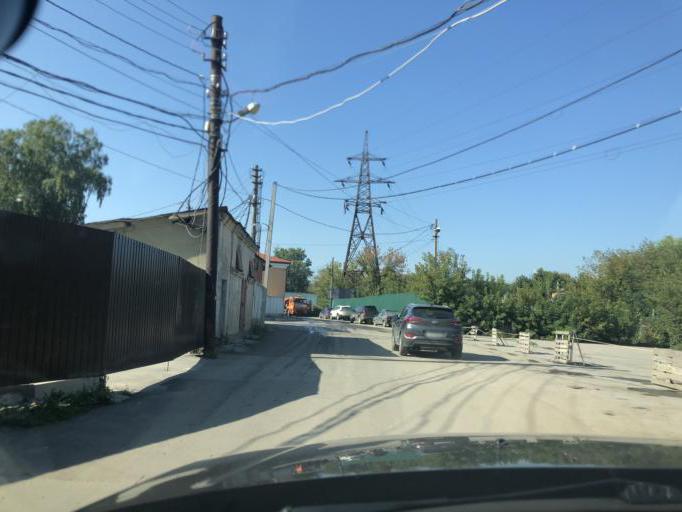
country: RU
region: Tula
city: Tula
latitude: 54.2026
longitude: 37.6288
